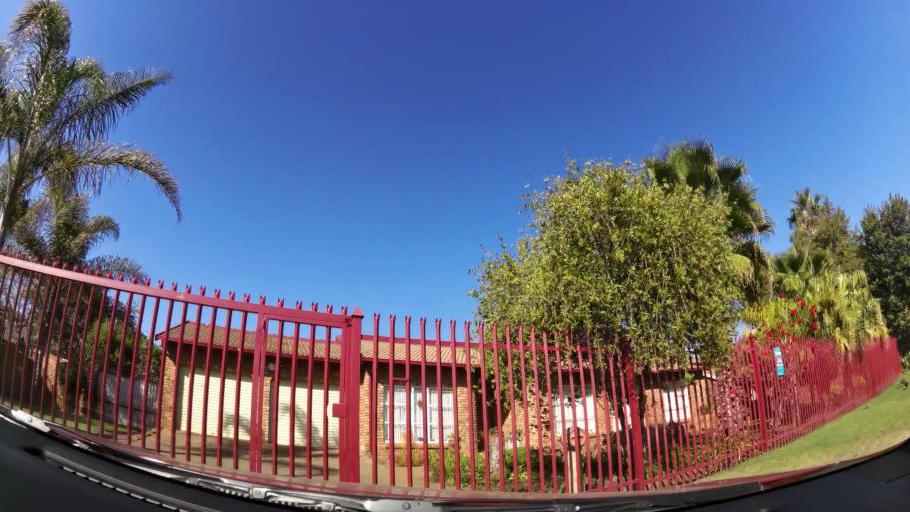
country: ZA
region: Gauteng
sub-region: City of Tshwane Metropolitan Municipality
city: Pretoria
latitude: -25.6803
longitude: 28.1414
